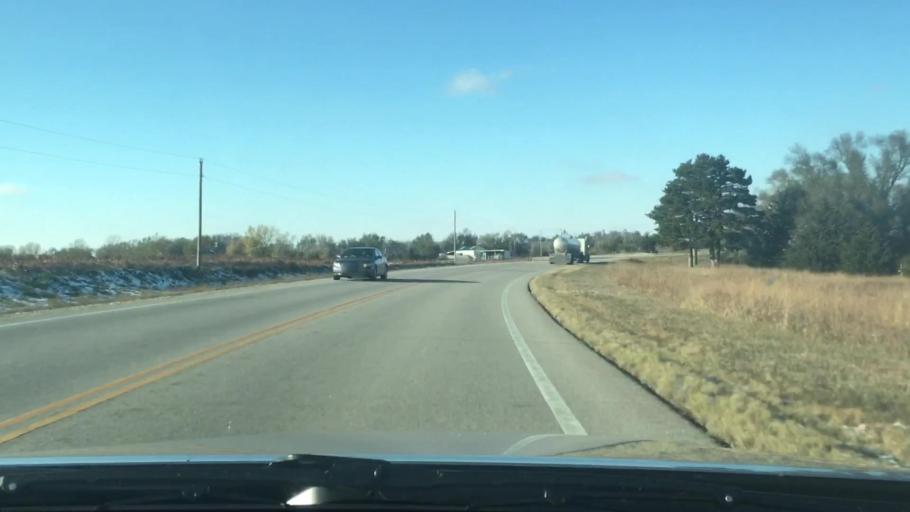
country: US
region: Kansas
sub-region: Rice County
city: Sterling
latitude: 38.1463
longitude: -98.2025
